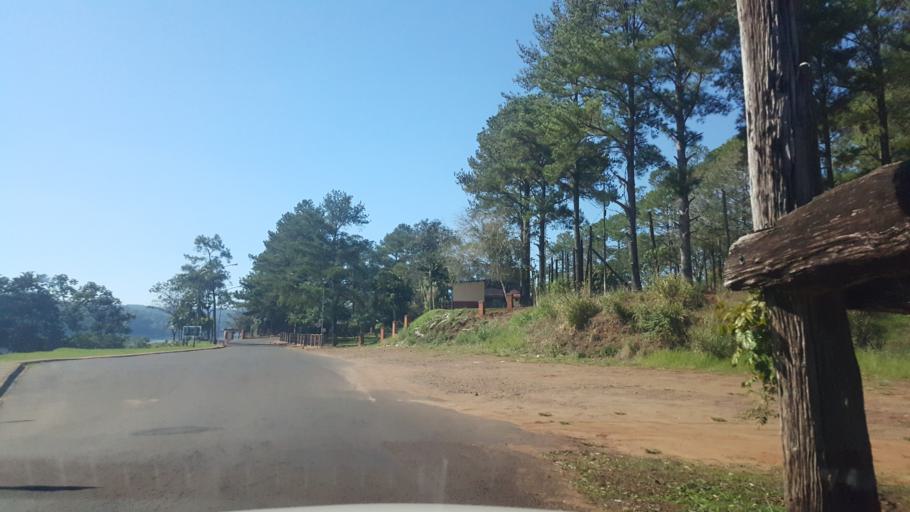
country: AR
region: Misiones
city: Puerto Rico
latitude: -26.7920
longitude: -55.0258
